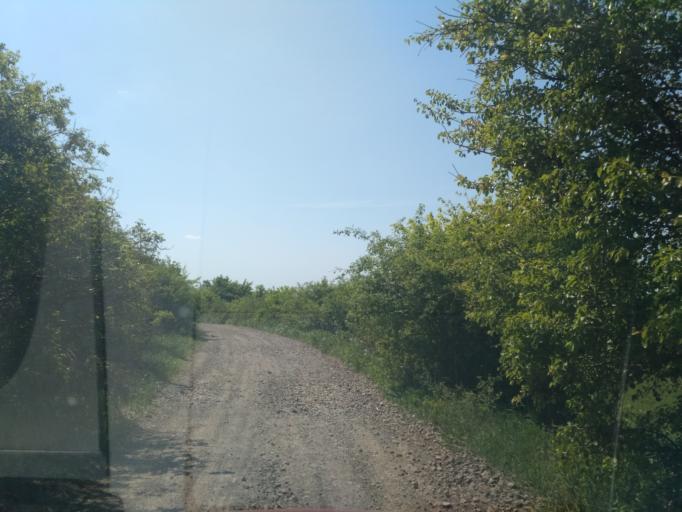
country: SK
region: Kosicky
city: Kosice
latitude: 48.8321
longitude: 21.4505
